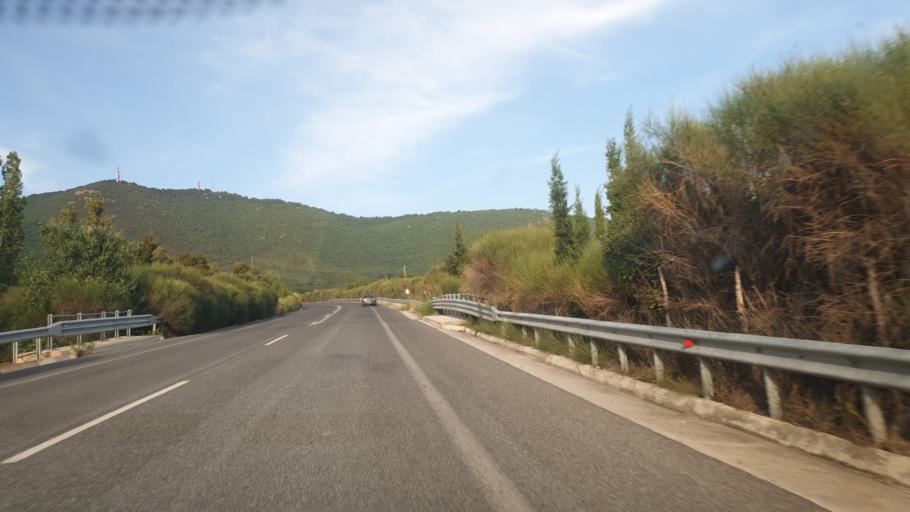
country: GR
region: Central Macedonia
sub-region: Nomos Chalkidikis
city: Polygyros
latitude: 40.3703
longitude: 23.4481
